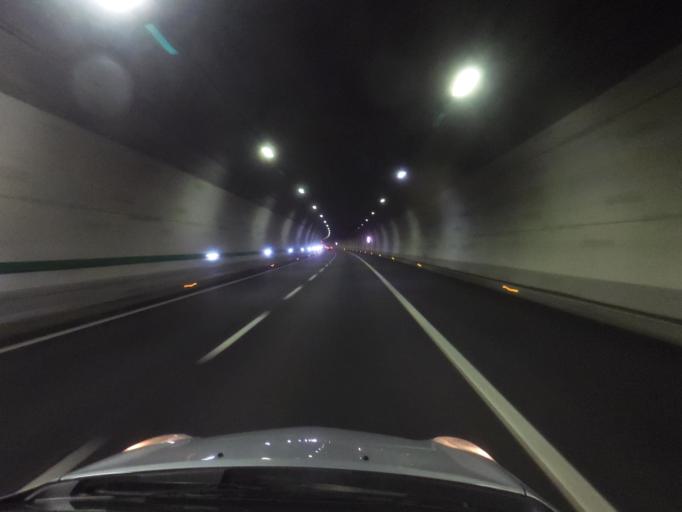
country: IT
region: Emilia-Romagna
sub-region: Provincia di Bologna
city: San Benedetto Val di Sambro
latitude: 44.1815
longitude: 11.1958
